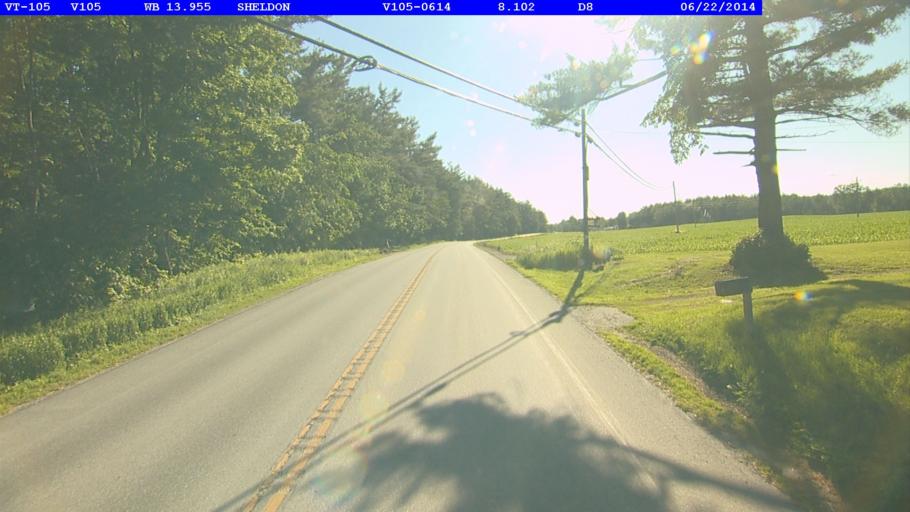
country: US
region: Vermont
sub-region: Franklin County
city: Enosburg Falls
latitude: 44.9102
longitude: -72.8778
